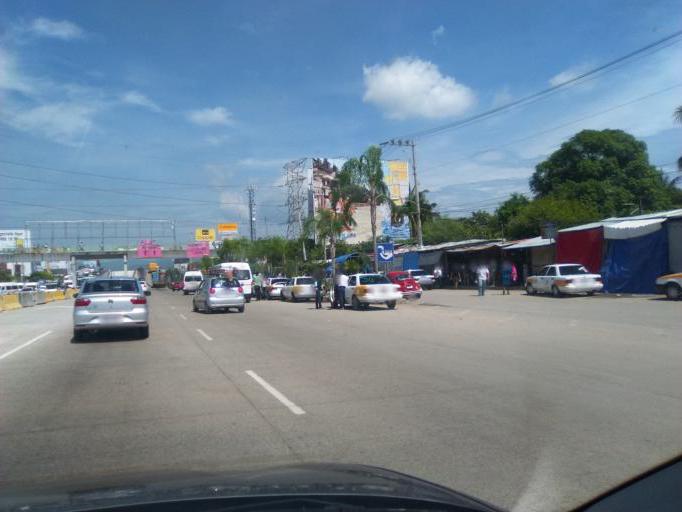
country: MX
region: Guerrero
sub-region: Acapulco de Juarez
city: Colonia Alborada
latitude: 16.8896
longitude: -99.8361
